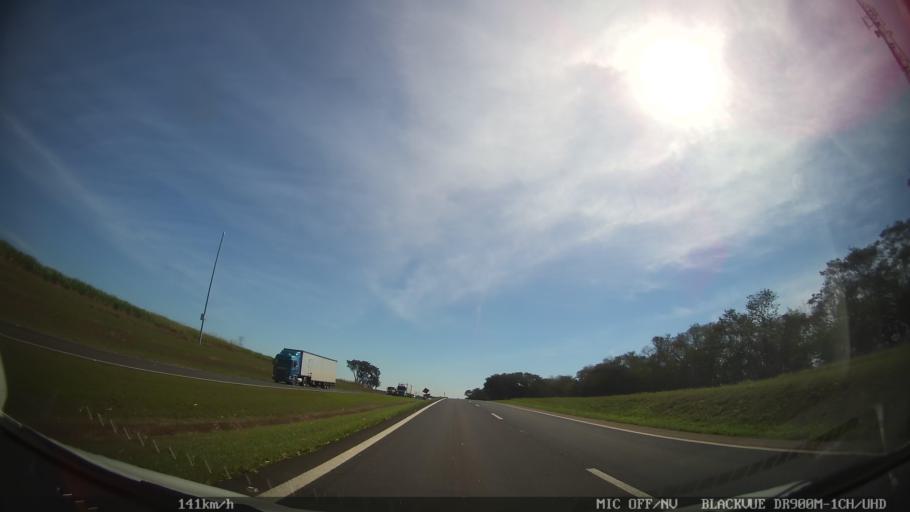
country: BR
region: Sao Paulo
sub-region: Porto Ferreira
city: Porto Ferreira
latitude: -21.9249
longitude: -47.4707
